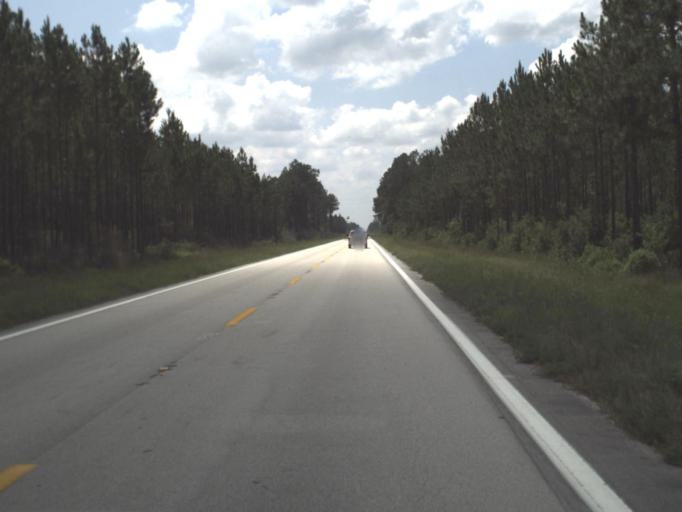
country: US
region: Florida
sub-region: Baker County
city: Macclenny
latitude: 30.5321
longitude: -82.3149
